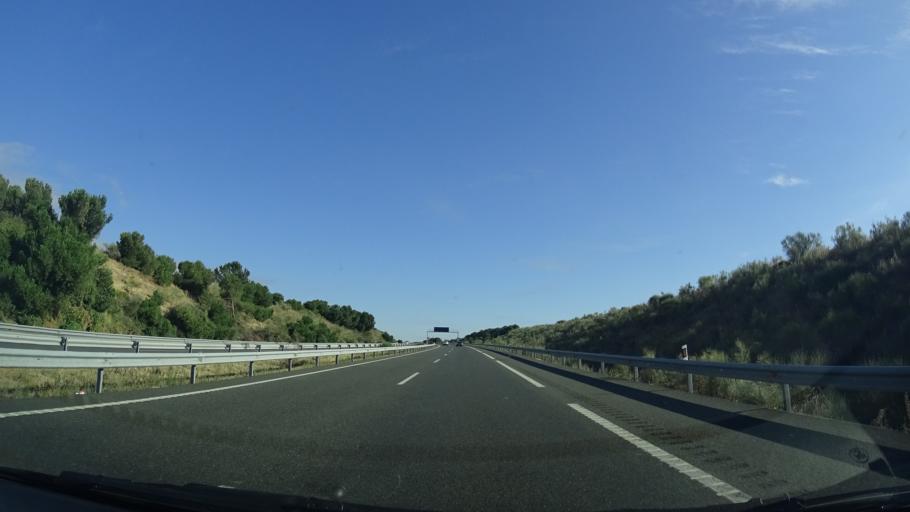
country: ES
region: Castille and Leon
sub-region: Provincia de Avila
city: Sanchidrian
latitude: 40.8730
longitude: -4.5670
